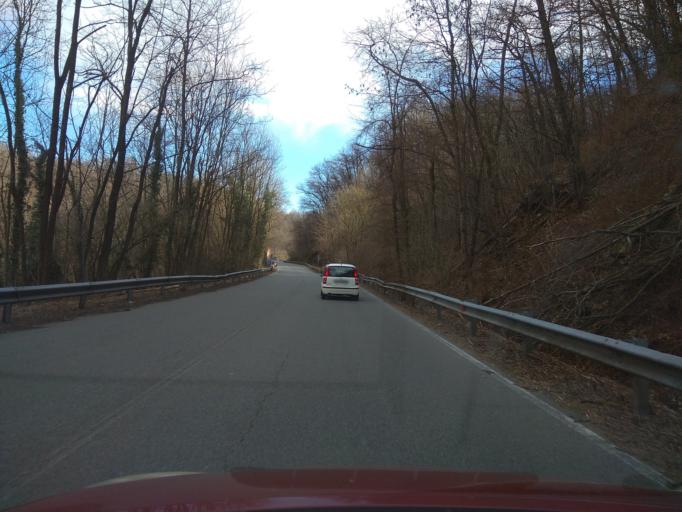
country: IT
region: Piedmont
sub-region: Provincia di Biella
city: Villa
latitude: 45.6083
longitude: 8.1785
